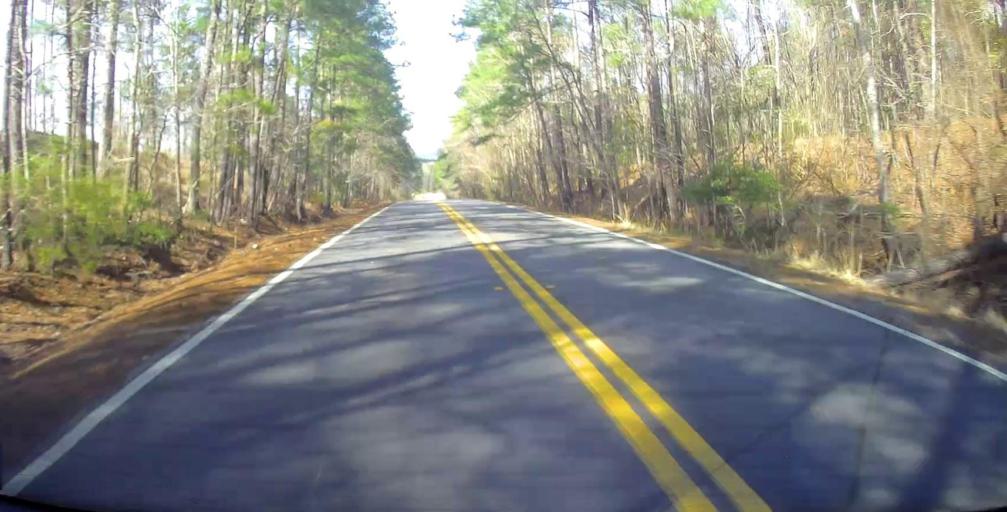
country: US
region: Georgia
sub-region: Twiggs County
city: Jeffersonville
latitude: 32.7531
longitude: -83.3435
